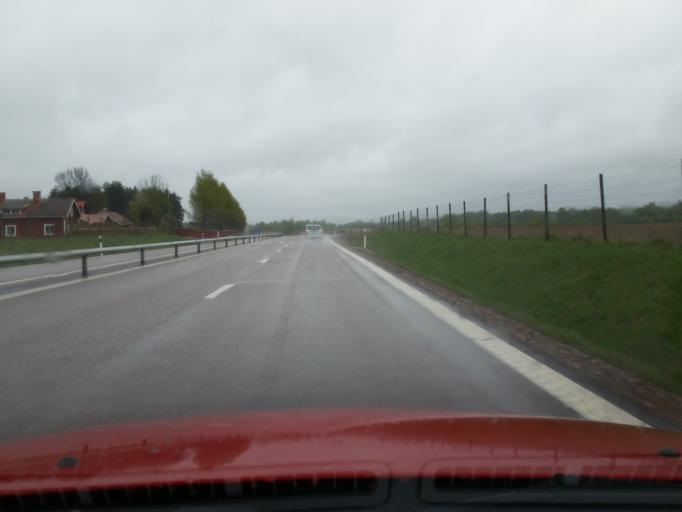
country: SE
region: Dalarna
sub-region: Saters Kommun
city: Saeter
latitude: 60.3327
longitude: 15.8304
